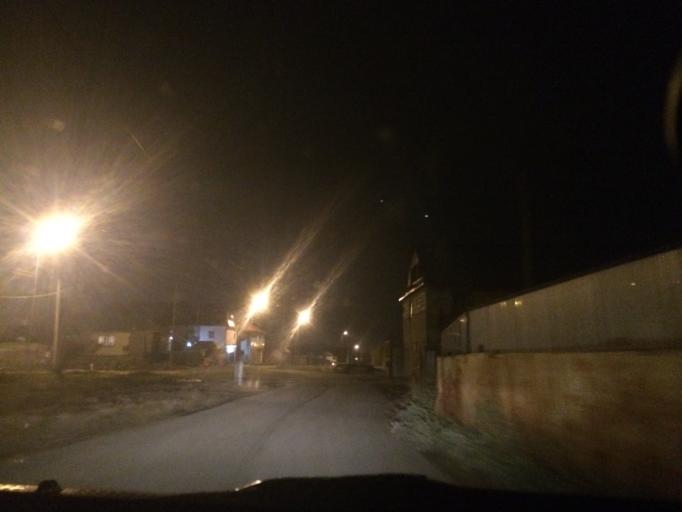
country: KZ
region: Astana Qalasy
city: Astana
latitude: 51.2002
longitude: 71.3722
